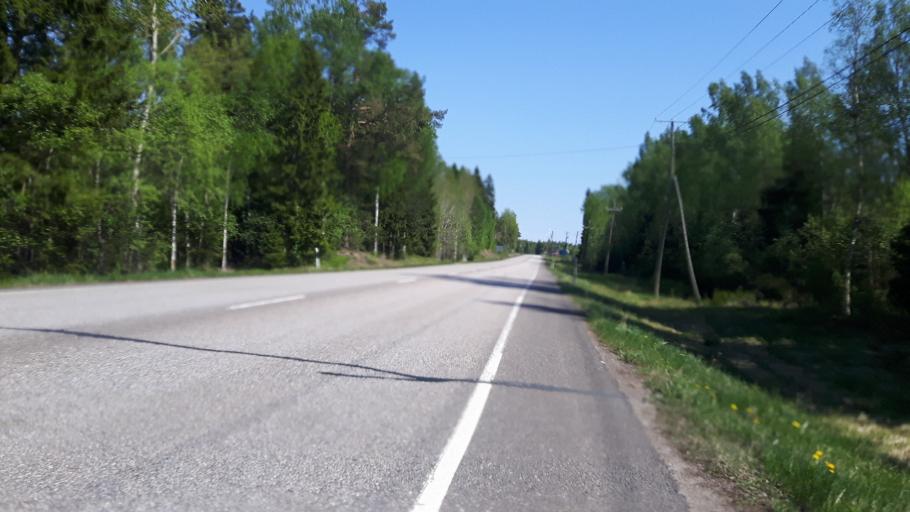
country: FI
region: Kymenlaakso
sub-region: Kotka-Hamina
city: Broby
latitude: 60.4891
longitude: 26.6540
